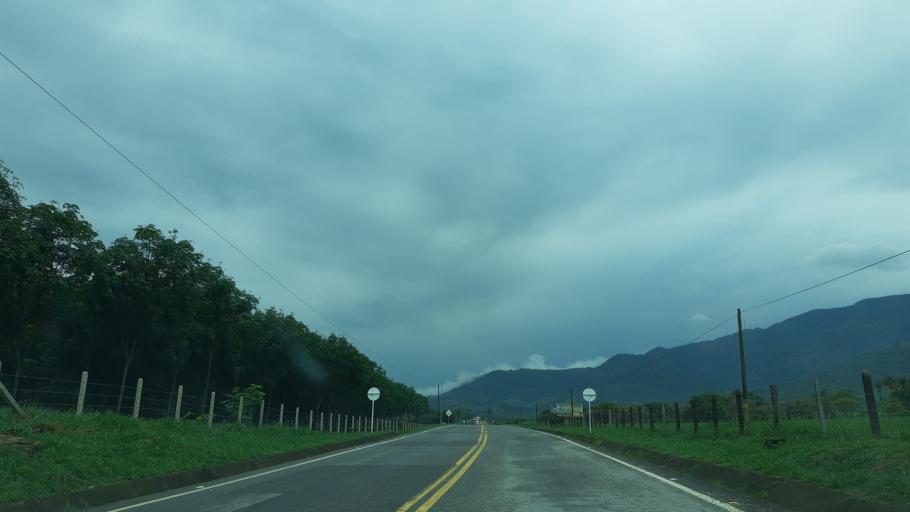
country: CO
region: Casanare
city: Monterrey
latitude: 4.8467
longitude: -72.9398
